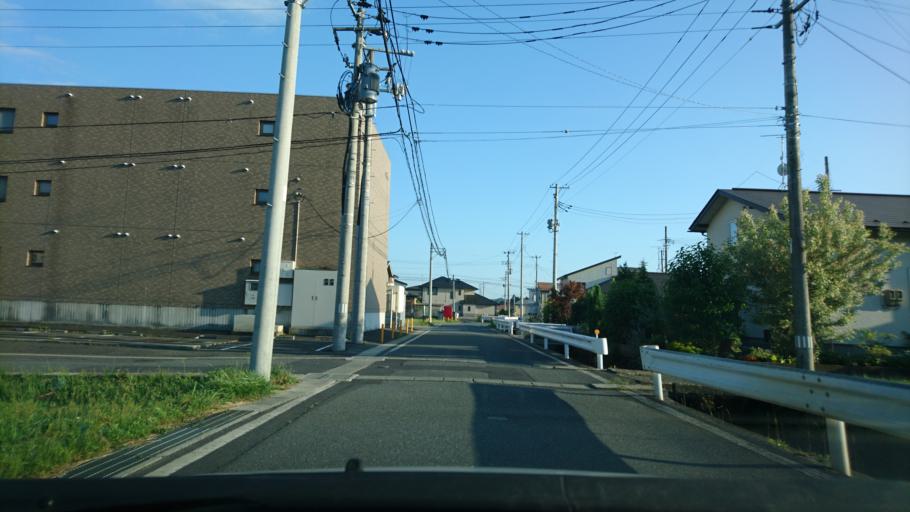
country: JP
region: Iwate
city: Ichinoseki
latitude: 38.9370
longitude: 141.1030
